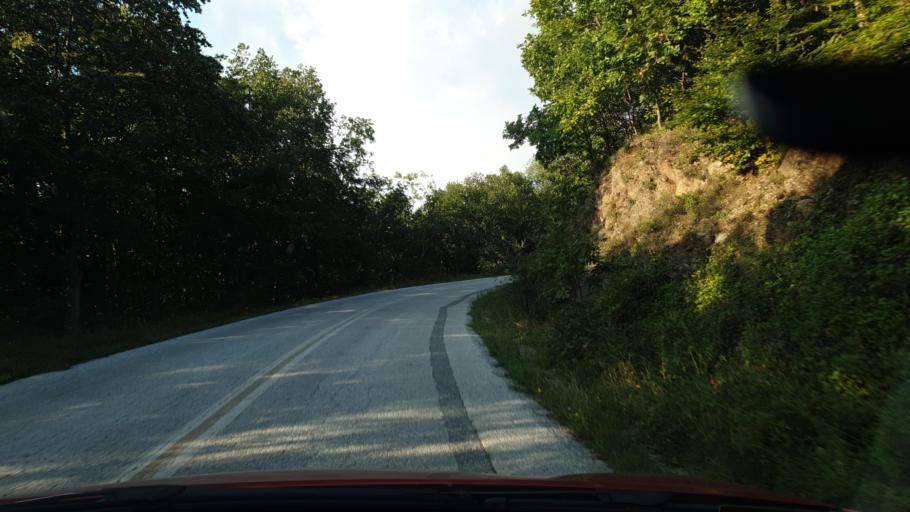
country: GR
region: Central Macedonia
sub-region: Nomos Chalkidikis
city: Galatista
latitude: 40.5086
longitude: 23.2497
